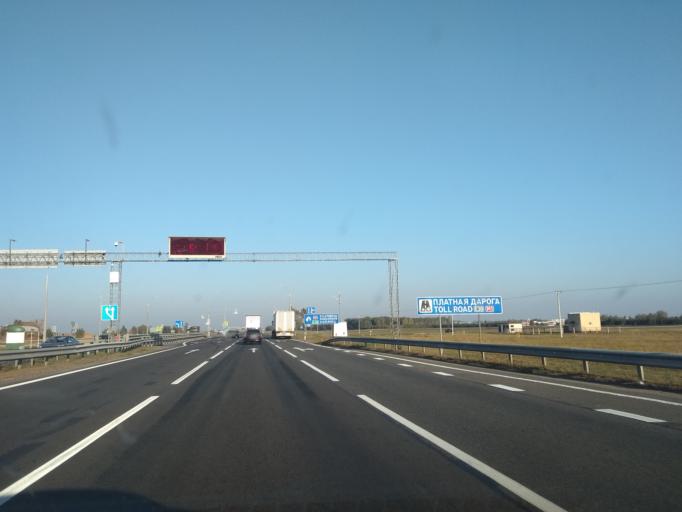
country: BY
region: Brest
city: Charnawchytsy
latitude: 52.1178
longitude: 23.8572
